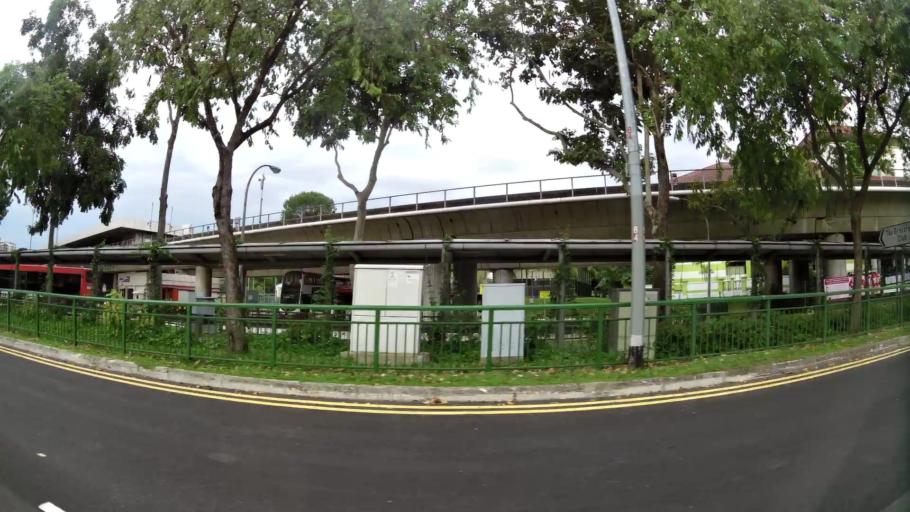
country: SG
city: Singapore
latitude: 1.3807
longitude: 103.8456
